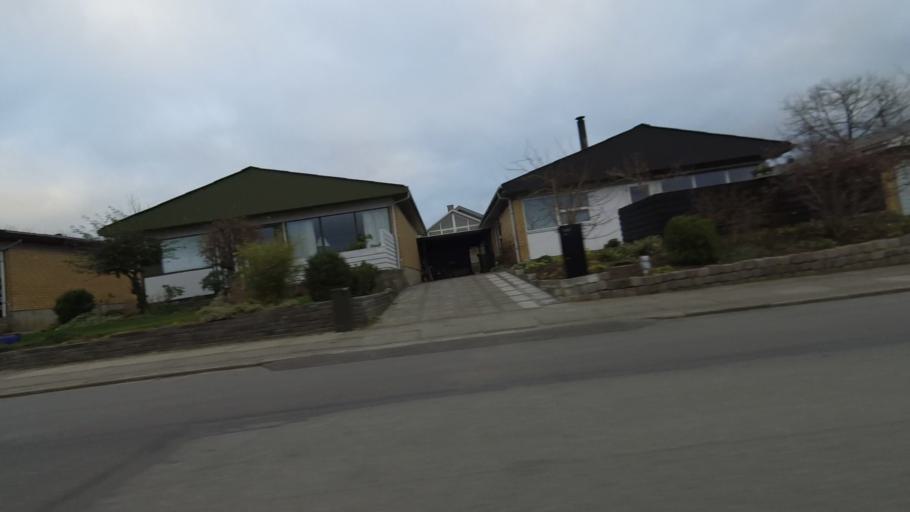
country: DK
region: Central Jutland
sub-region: Arhus Kommune
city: Stavtrup
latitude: 56.1604
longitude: 10.1048
